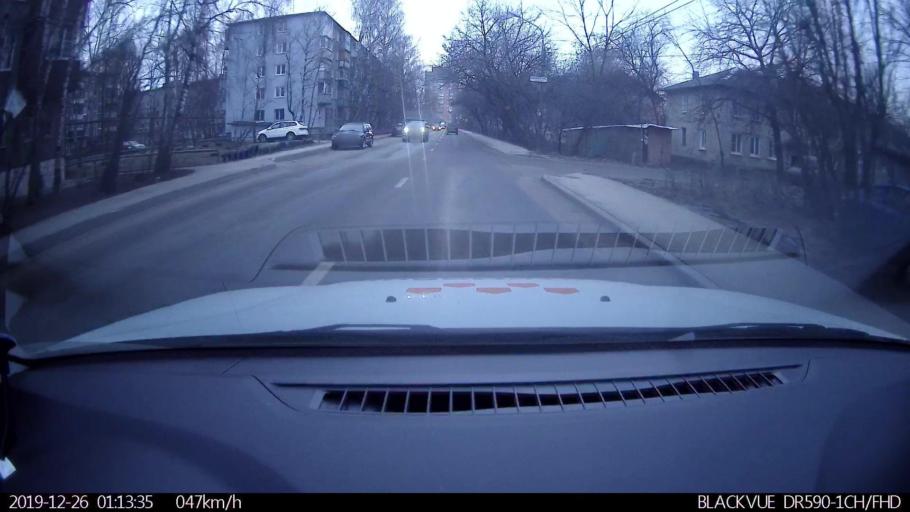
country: RU
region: Nizjnij Novgorod
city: Nizhniy Novgorod
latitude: 56.2775
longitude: 43.9105
